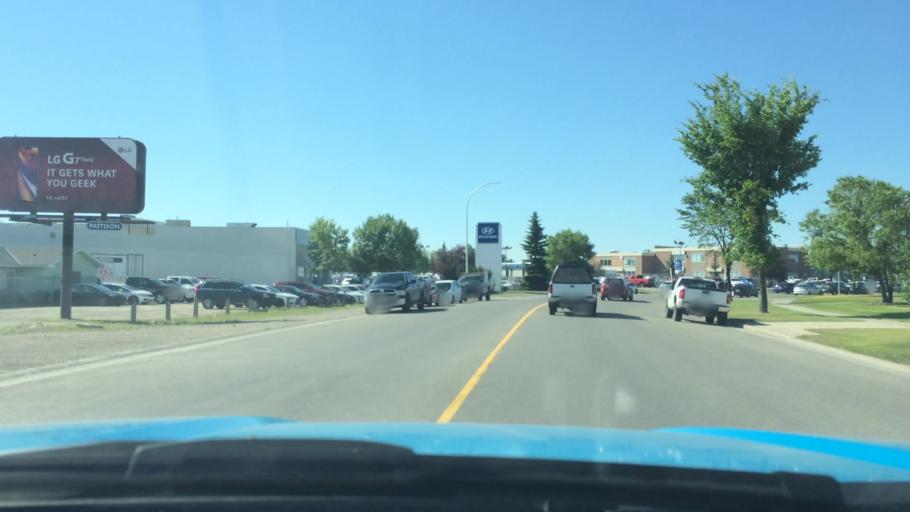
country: CA
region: Alberta
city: Calgary
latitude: 51.0707
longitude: -114.0042
